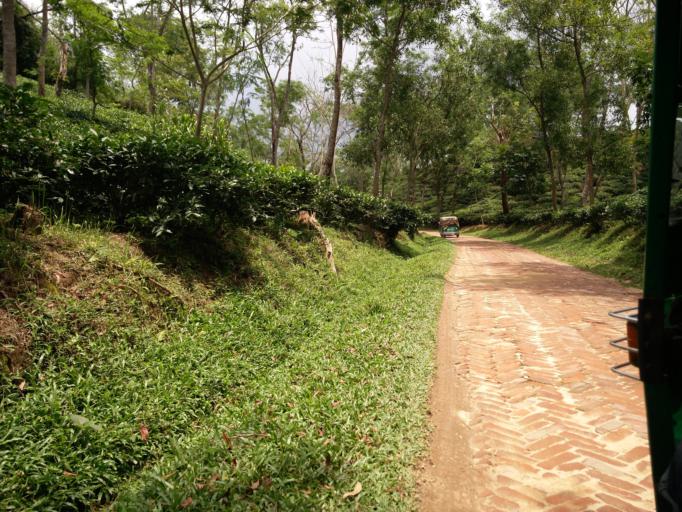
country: IN
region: Tripura
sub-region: Dhalai
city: Kamalpur
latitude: 24.2992
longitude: 91.7975
